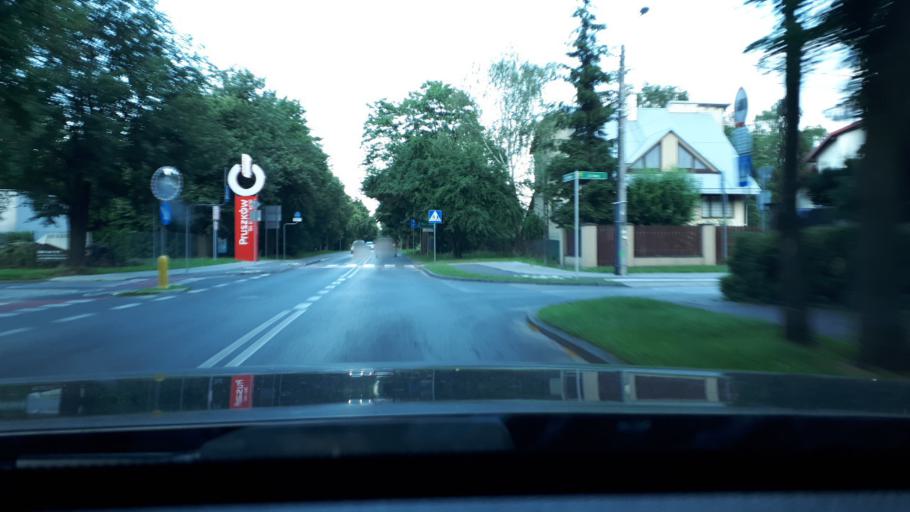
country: PL
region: Masovian Voivodeship
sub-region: Powiat pruszkowski
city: Komorow
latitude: 52.1582
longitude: 20.8237
